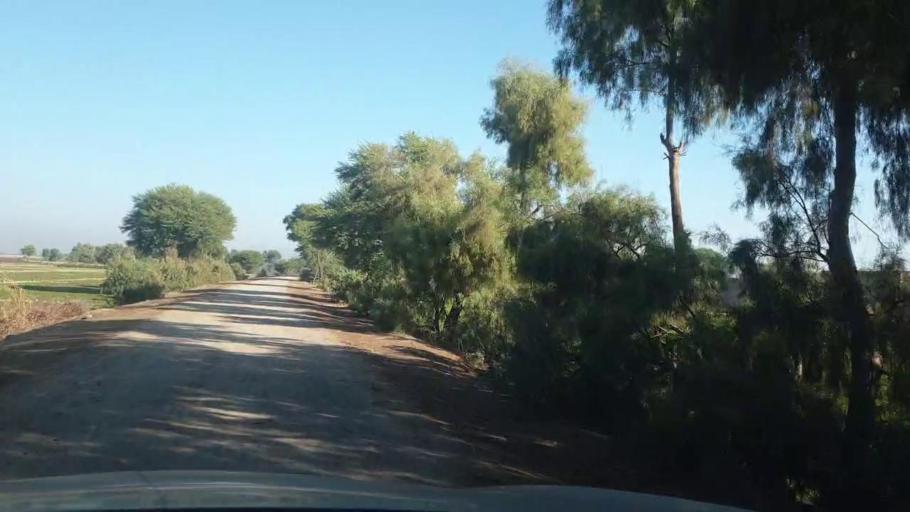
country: PK
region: Sindh
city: Bhan
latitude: 26.5374
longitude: 67.6894
